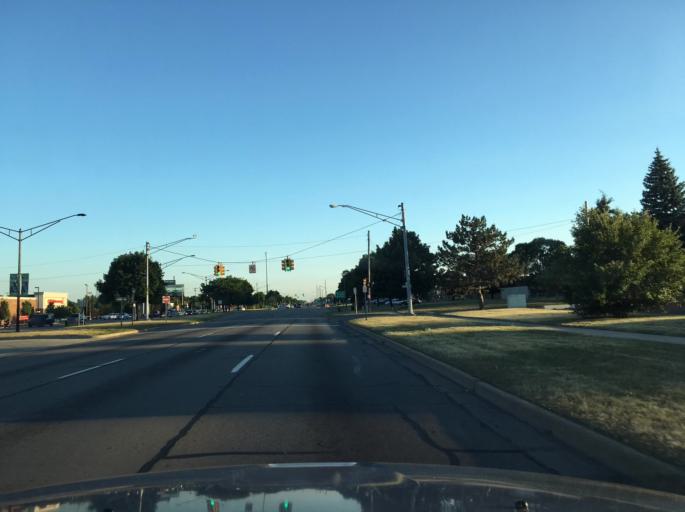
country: US
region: Michigan
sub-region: Macomb County
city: Mount Clemens
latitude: 42.5725
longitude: -82.8904
